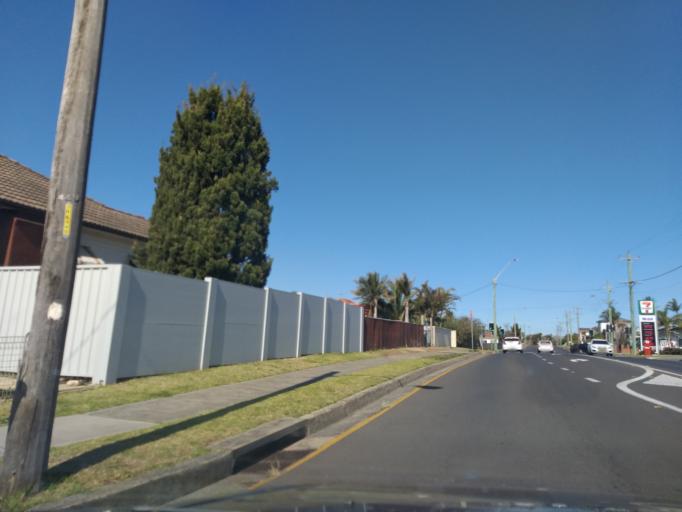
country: AU
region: New South Wales
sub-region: Wollongong
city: Corrimal
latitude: -34.3836
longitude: 150.9070
